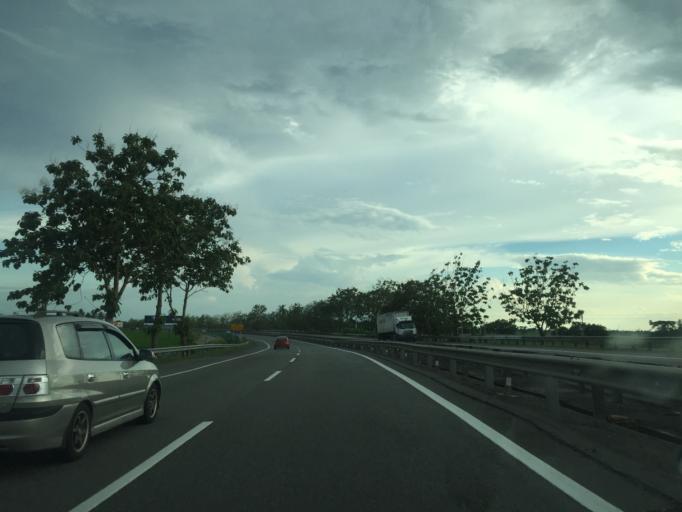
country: MY
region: Kedah
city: Alor Setar
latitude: 6.0203
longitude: 100.4149
